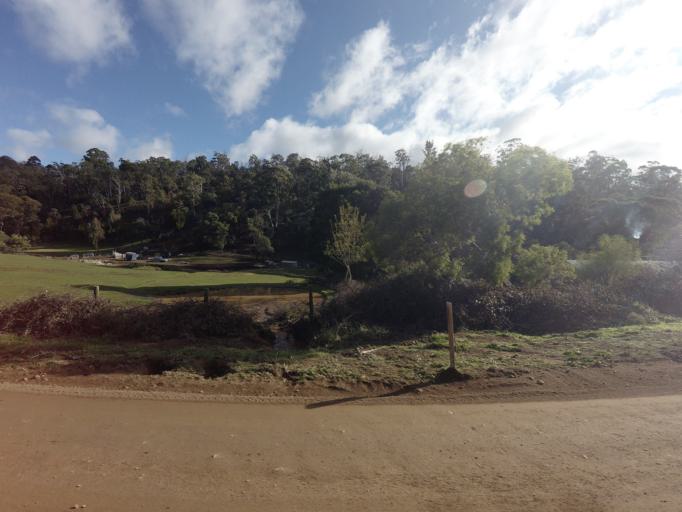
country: AU
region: Tasmania
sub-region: Derwent Valley
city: New Norfolk
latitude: -42.8068
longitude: 147.1356
